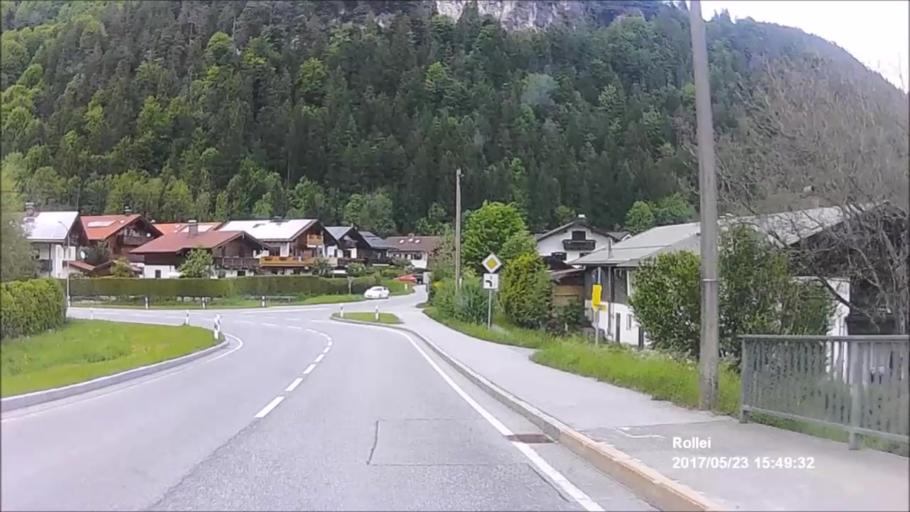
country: DE
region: Bavaria
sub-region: Upper Bavaria
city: Bischofswiesen
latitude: 47.6534
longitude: 12.9598
